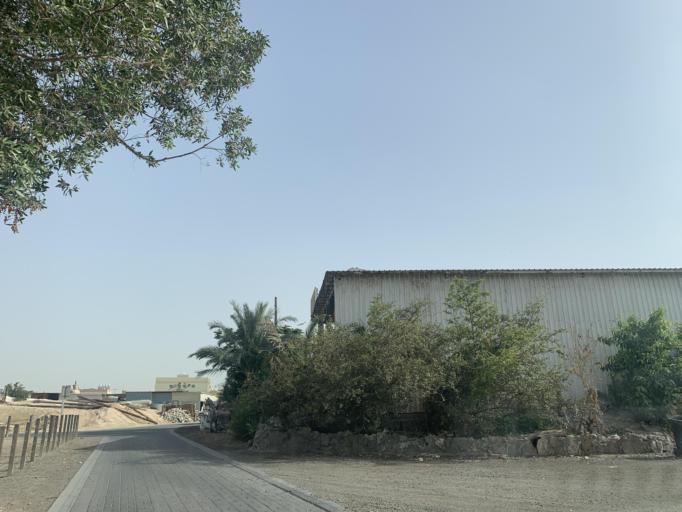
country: BH
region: Northern
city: Madinat `Isa
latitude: 26.1607
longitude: 50.5167
